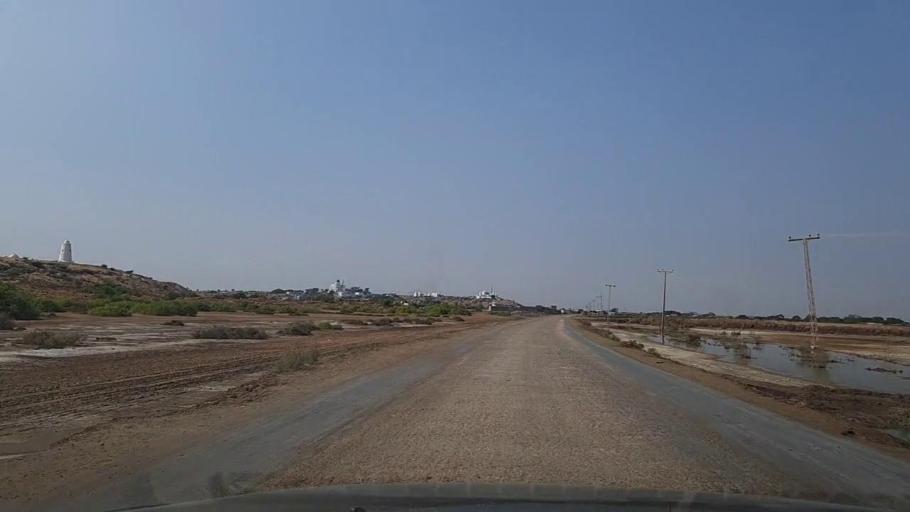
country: PK
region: Sindh
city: Chuhar Jamali
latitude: 24.5546
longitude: 67.8890
